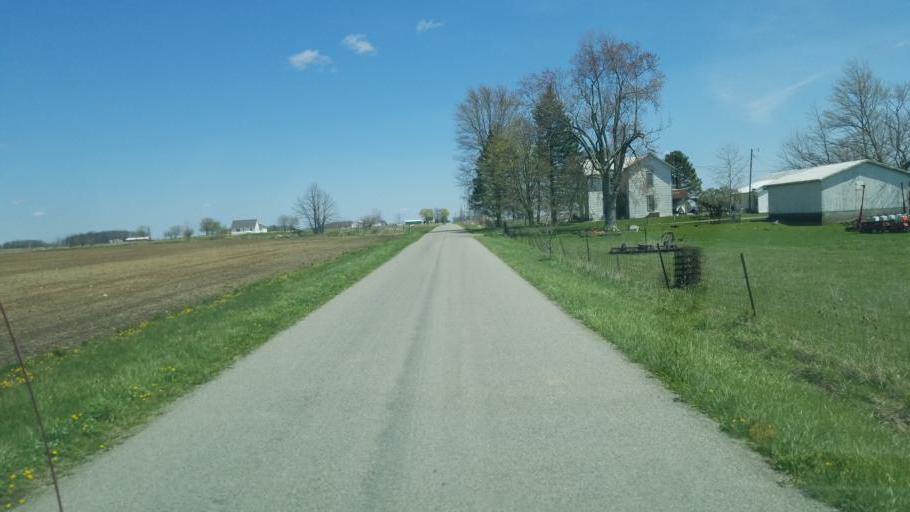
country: US
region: Ohio
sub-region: Union County
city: Richwood
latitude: 40.4912
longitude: -83.2850
